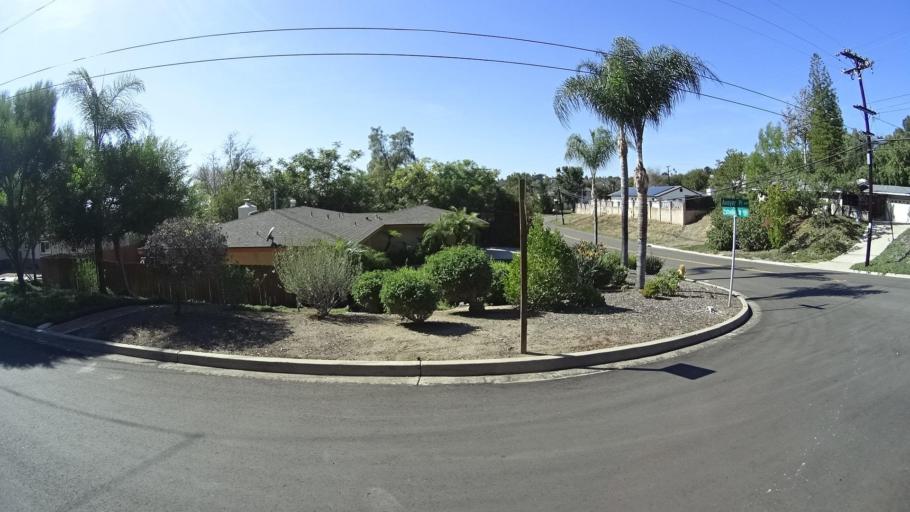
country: US
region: California
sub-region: San Diego County
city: Casa de Oro-Mount Helix
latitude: 32.7529
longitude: -116.9791
